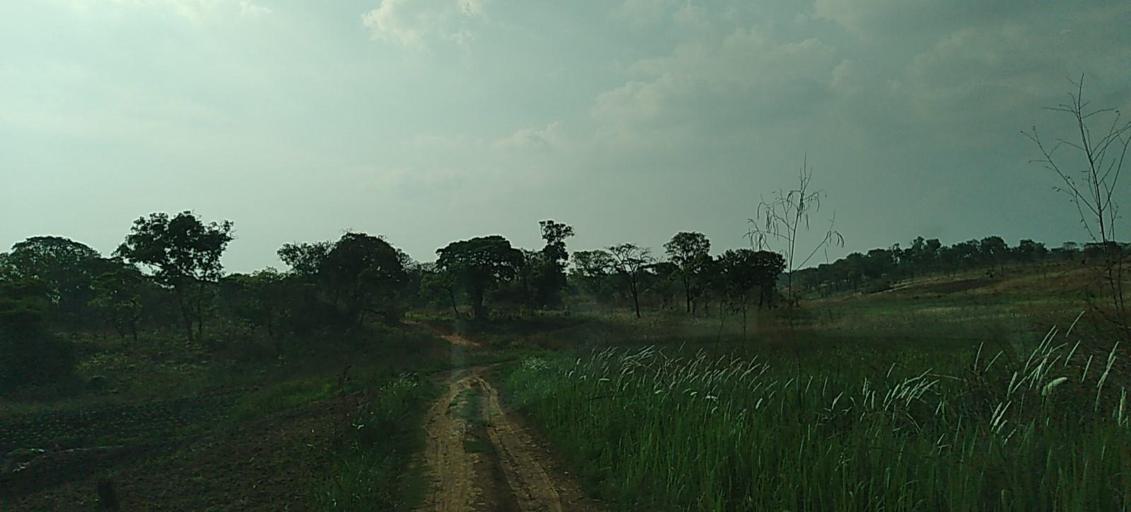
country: ZM
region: North-Western
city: Solwezi
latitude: -12.0662
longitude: 26.1779
